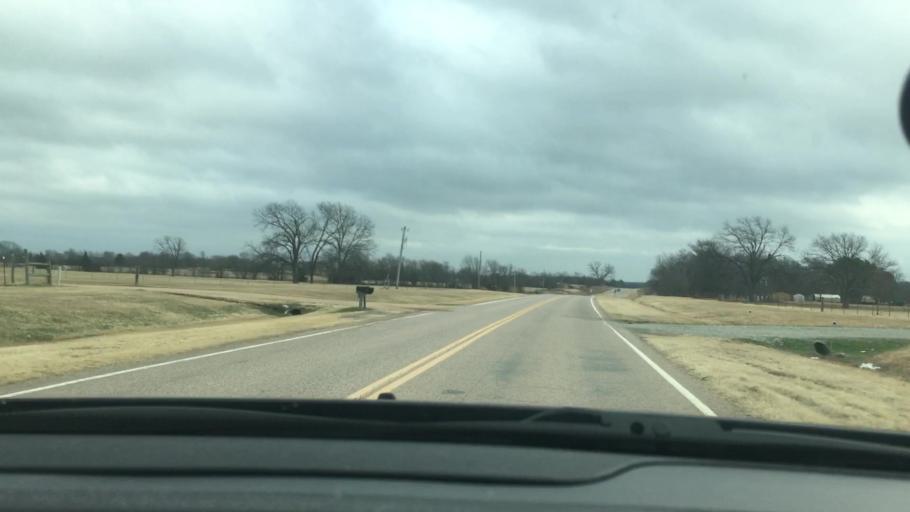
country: US
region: Oklahoma
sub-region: Bryan County
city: Durant
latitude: 34.0854
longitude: -96.4026
